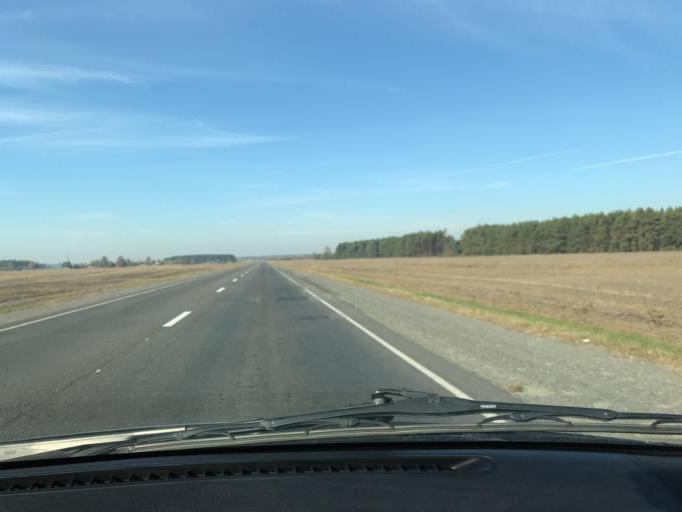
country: BY
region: Brest
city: Davyd-Haradok
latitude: 52.2398
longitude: 27.2080
